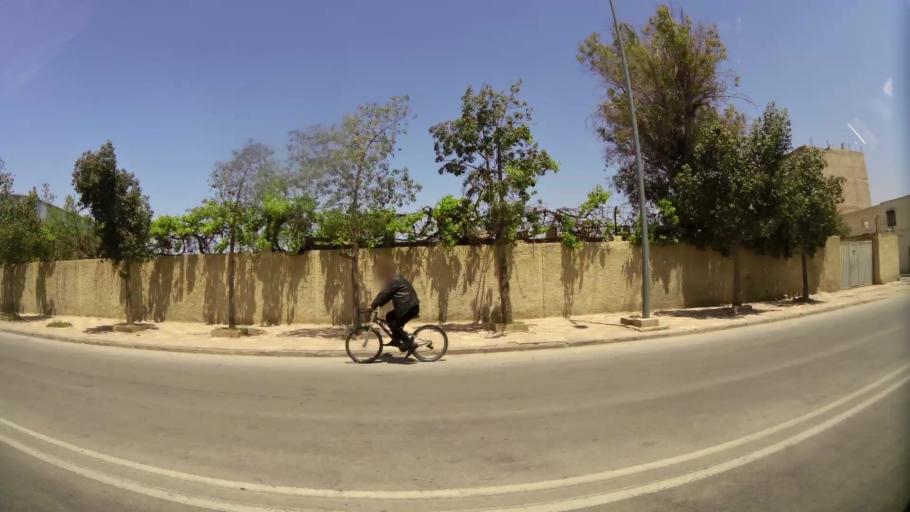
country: MA
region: Oriental
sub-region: Oujda-Angad
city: Oujda
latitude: 34.7002
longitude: -1.8935
